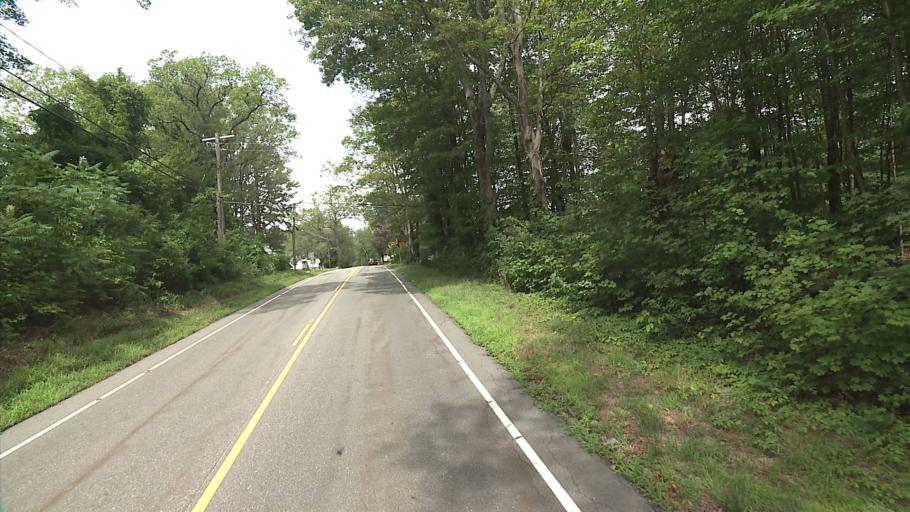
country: US
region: Massachusetts
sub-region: Hampden County
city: Holland
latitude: 41.9534
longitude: -72.1050
